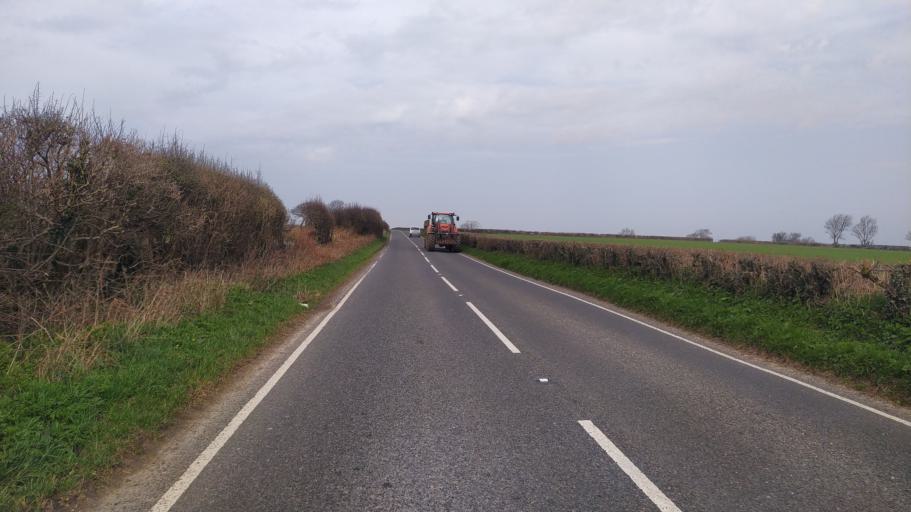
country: GB
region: England
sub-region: Dorset
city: Beaminster
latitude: 50.8232
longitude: -2.6702
